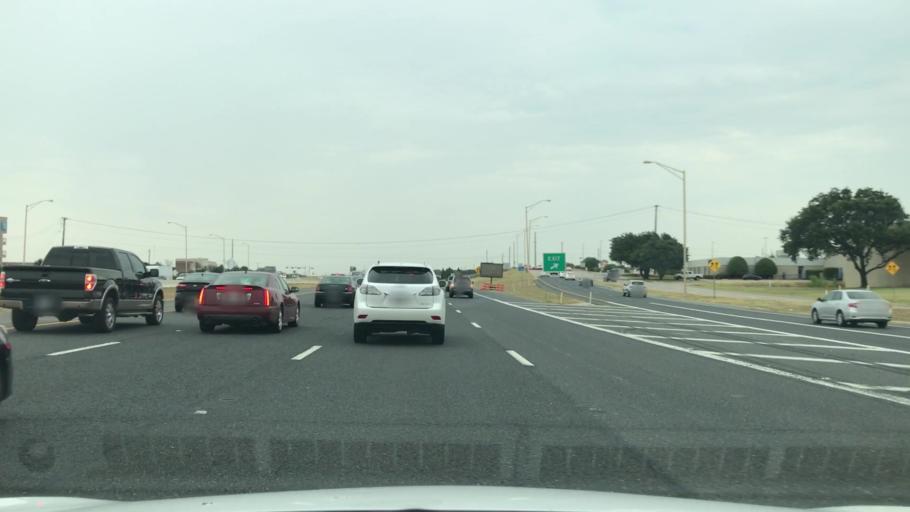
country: US
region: Texas
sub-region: Dallas County
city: Carrollton
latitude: 32.9831
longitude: -96.9157
